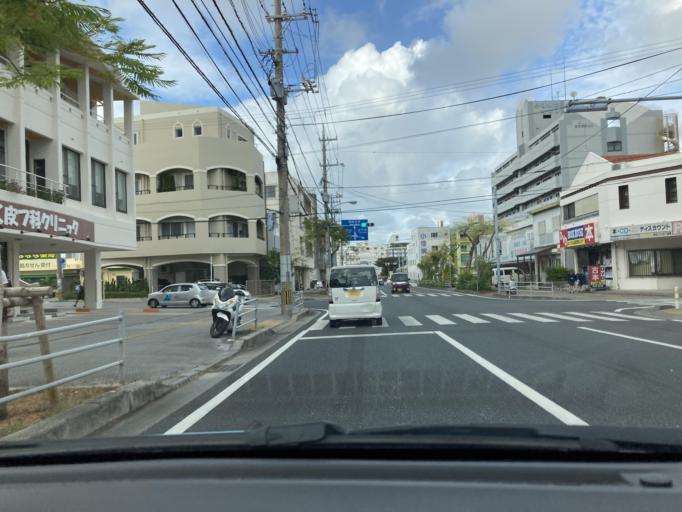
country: JP
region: Okinawa
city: Tomigusuku
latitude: 26.1924
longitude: 127.6755
